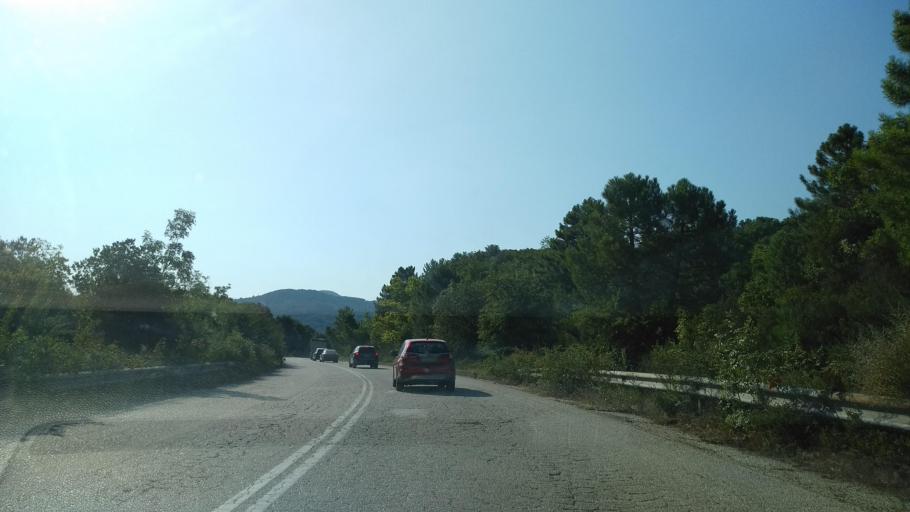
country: GR
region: Central Macedonia
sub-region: Nomos Chalkidikis
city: Stratonion
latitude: 40.5615
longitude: 23.8217
